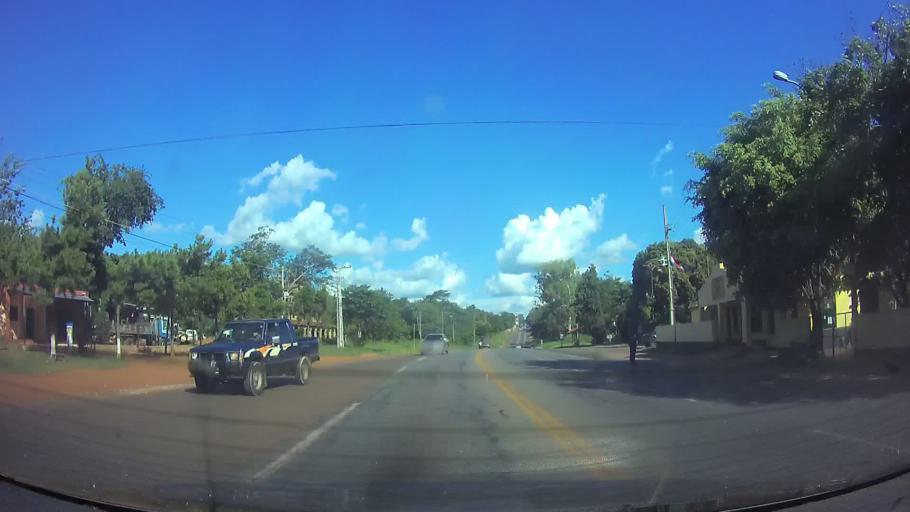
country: PY
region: Cordillera
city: Eusebio Ayala
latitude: -25.3917
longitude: -56.9576
